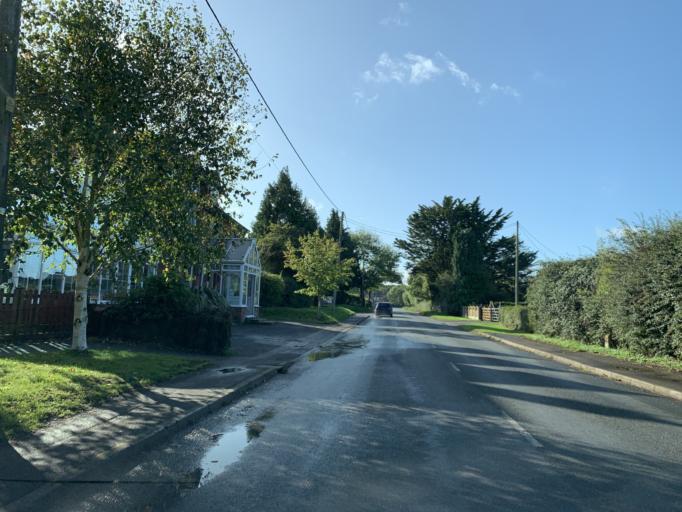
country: GB
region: England
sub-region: Wiltshire
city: Downton
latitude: 50.9780
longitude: -1.7193
